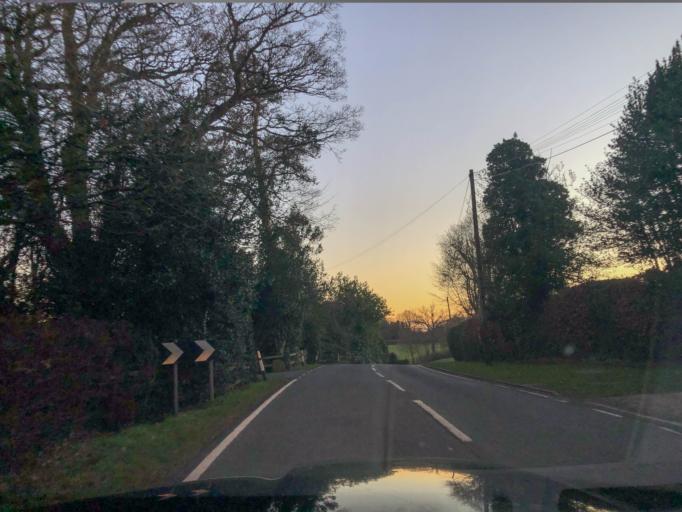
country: GB
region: England
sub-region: Warwickshire
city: Kenilworth
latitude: 52.3266
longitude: -1.5858
